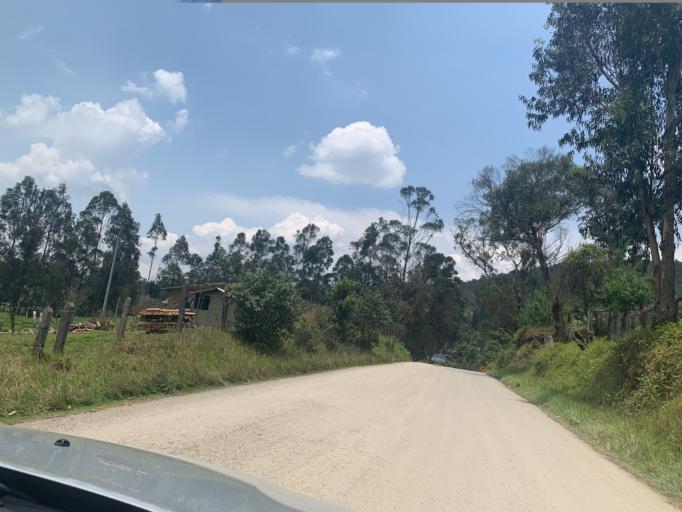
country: CO
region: Boyaca
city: Chiquinquira
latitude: 5.5540
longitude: -73.7487
